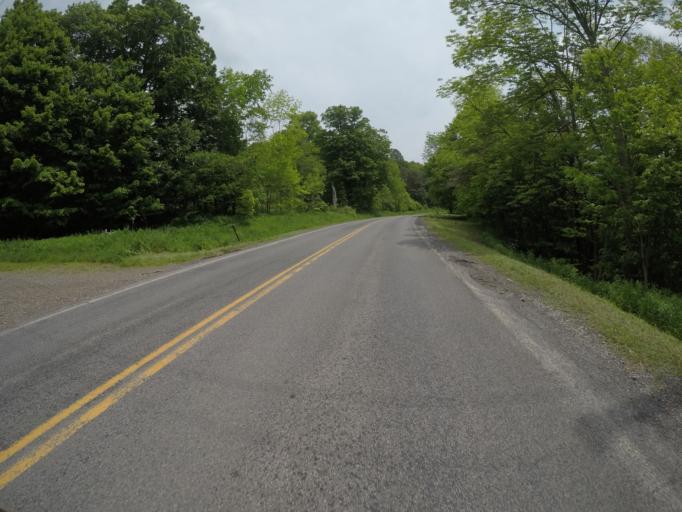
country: US
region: New York
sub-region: Delaware County
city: Stamford
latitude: 42.2722
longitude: -74.7343
